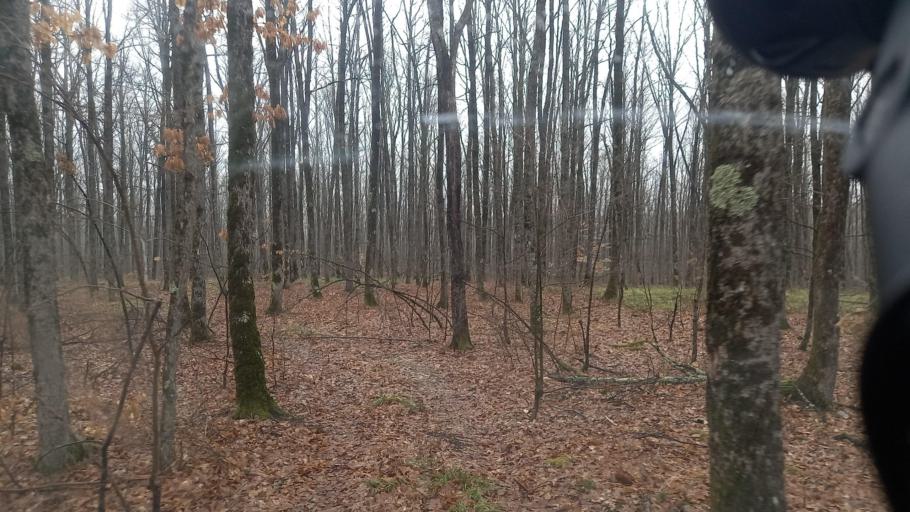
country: RU
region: Krasnodarskiy
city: Saratovskaya
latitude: 44.6531
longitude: 39.2402
